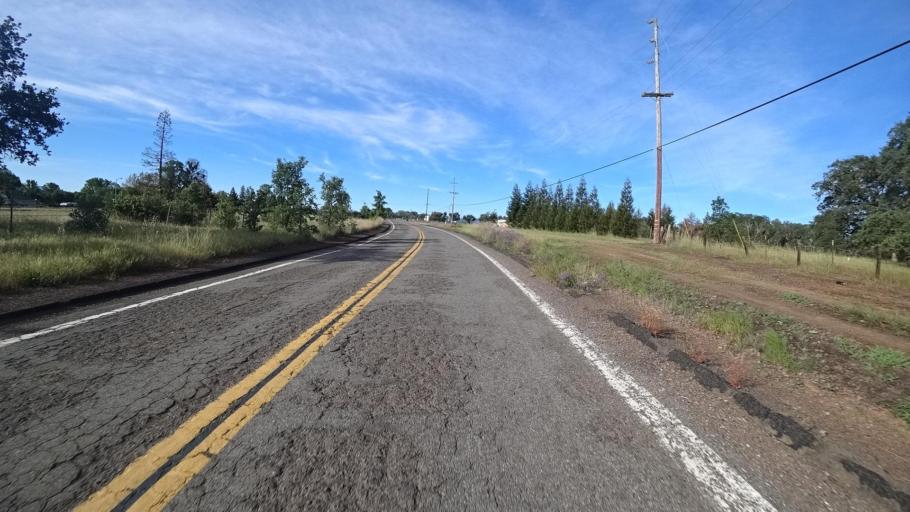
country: US
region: California
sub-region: Lake County
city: North Lakeport
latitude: 39.0807
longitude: -122.9308
